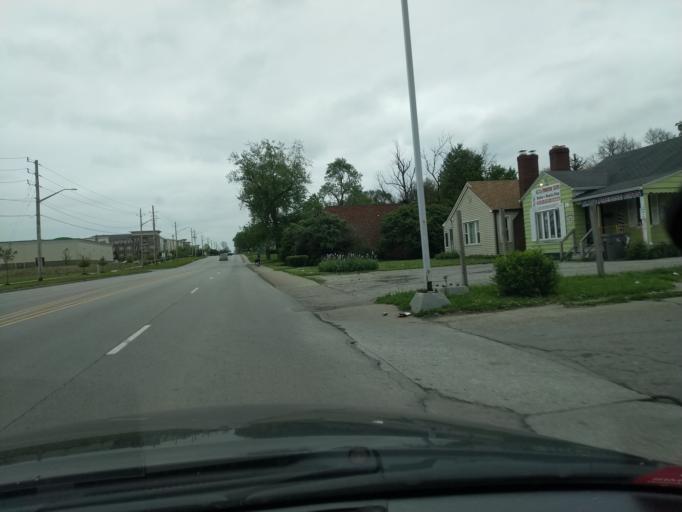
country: US
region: Indiana
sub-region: Marion County
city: Broad Ripple
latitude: 39.8253
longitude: -86.1146
